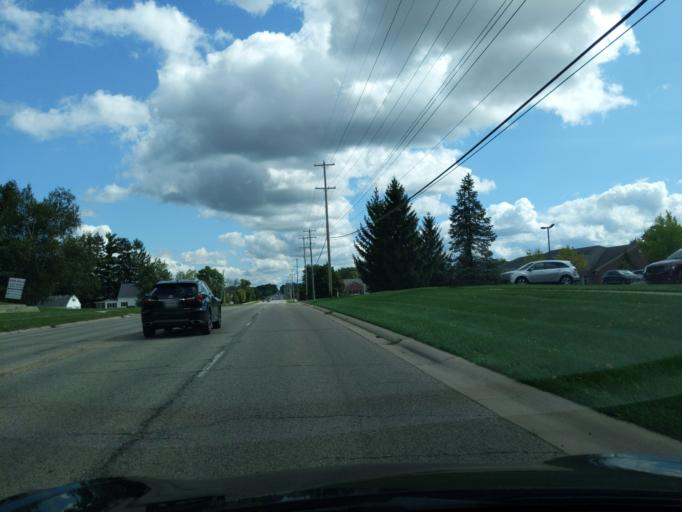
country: US
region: Michigan
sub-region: Ingham County
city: Okemos
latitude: 42.6829
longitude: -84.4438
